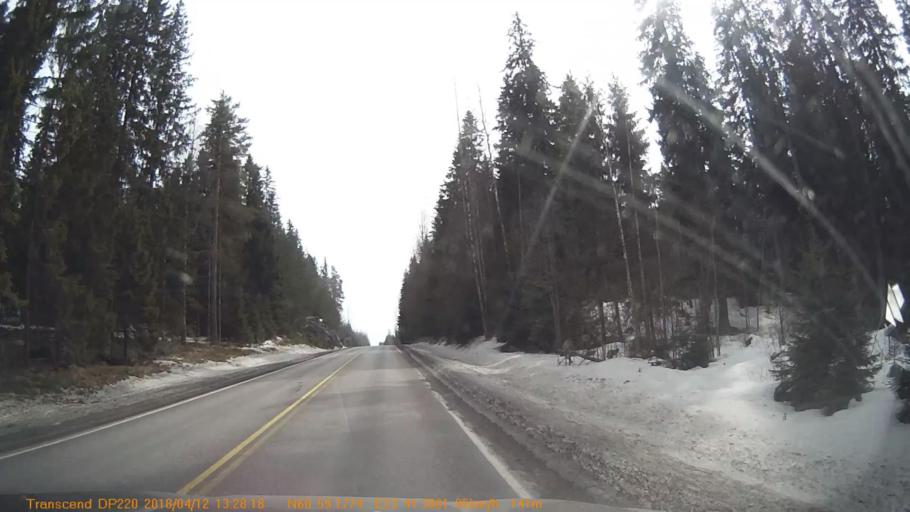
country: FI
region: Pirkanmaa
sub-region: Etelae-Pirkanmaa
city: Kylmaekoski
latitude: 60.9861
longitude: 23.6886
